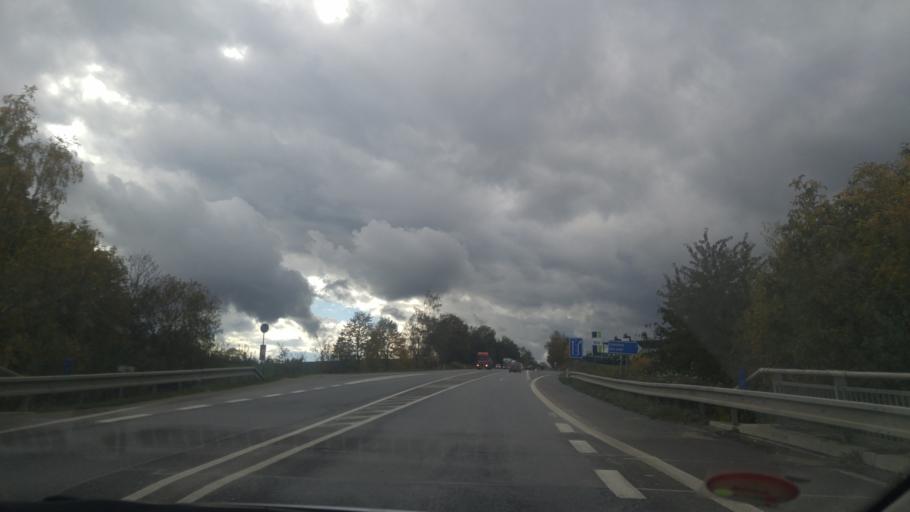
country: CZ
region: Jihocesky
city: Sevetin
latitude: 49.1266
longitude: 14.6041
